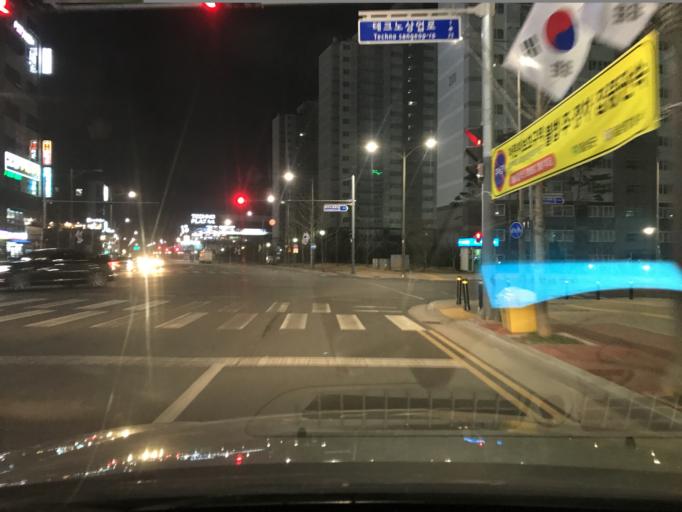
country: KR
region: Daegu
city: Hwawon
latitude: 35.6915
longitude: 128.4534
